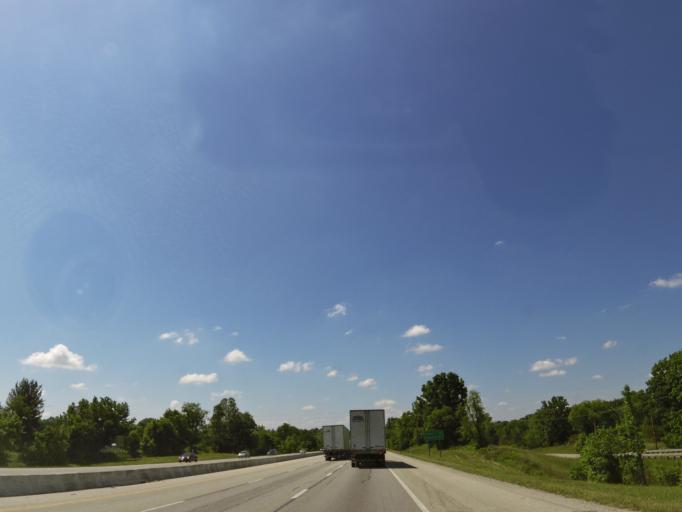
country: US
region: Kentucky
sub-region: Laurel County
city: London
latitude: 37.0800
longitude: -84.0996
